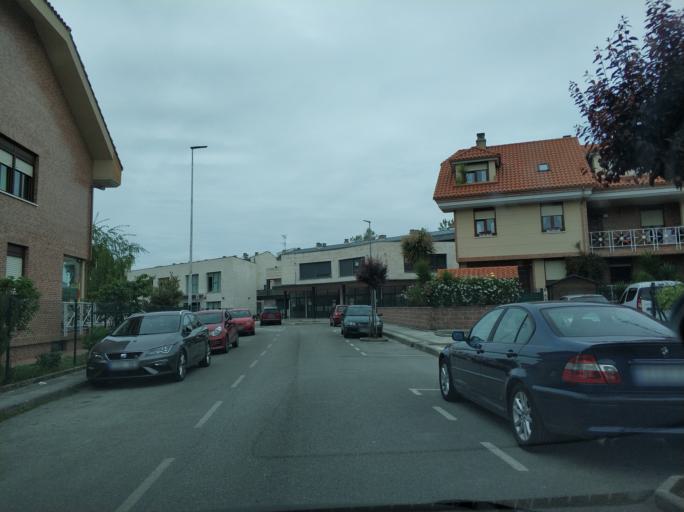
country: ES
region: Cantabria
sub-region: Provincia de Cantabria
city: Puente Viesgo
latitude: 43.3550
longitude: -3.9515
